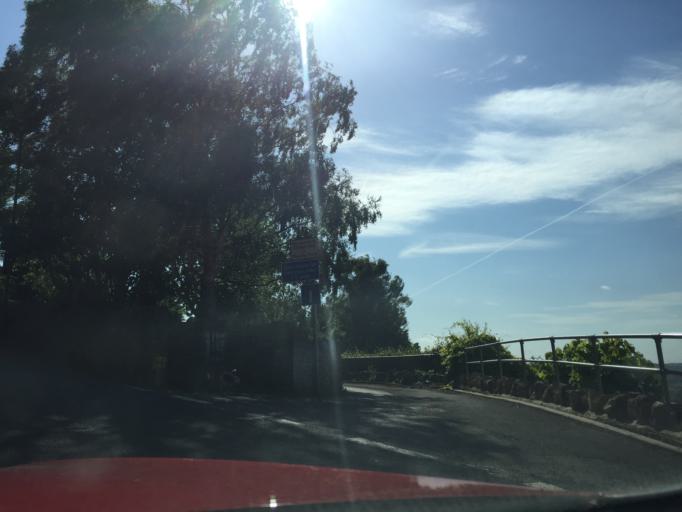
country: GB
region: England
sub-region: Gloucestershire
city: Stonehouse
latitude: 51.7595
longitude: -2.2497
